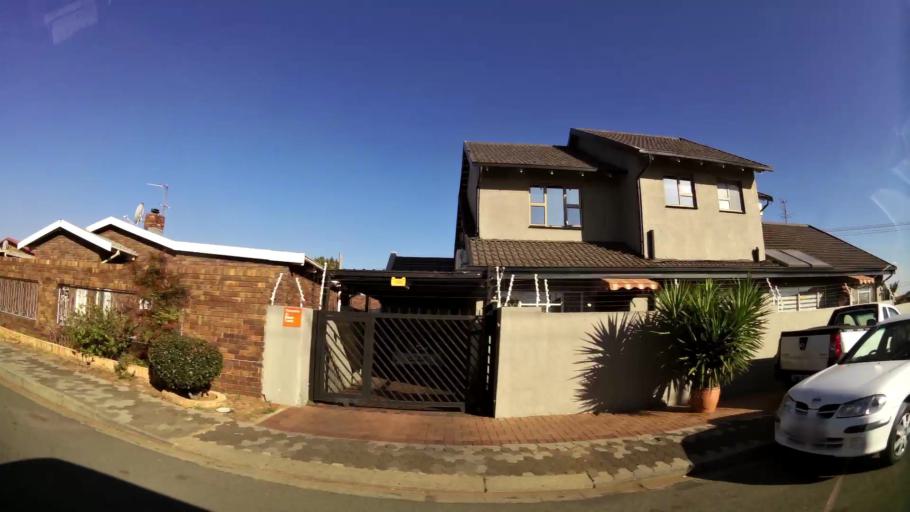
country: ZA
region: Gauteng
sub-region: City of Johannesburg Metropolitan Municipality
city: Johannesburg
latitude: -26.2133
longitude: 27.9812
